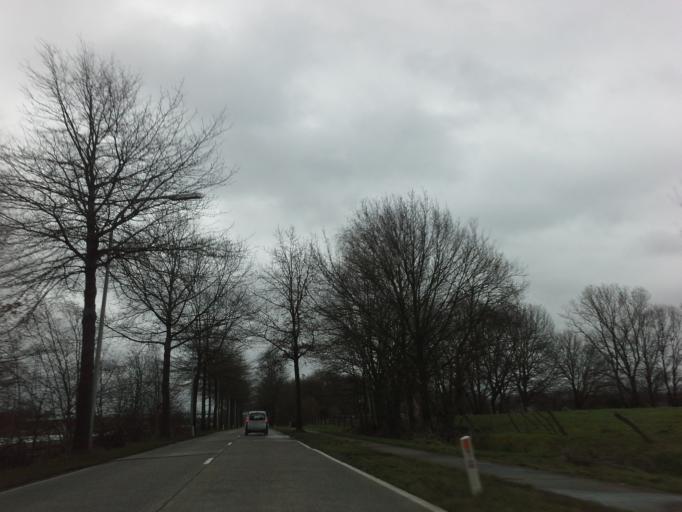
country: BE
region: Flanders
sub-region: Provincie Antwerpen
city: Meerhout
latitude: 51.1080
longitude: 5.0461
